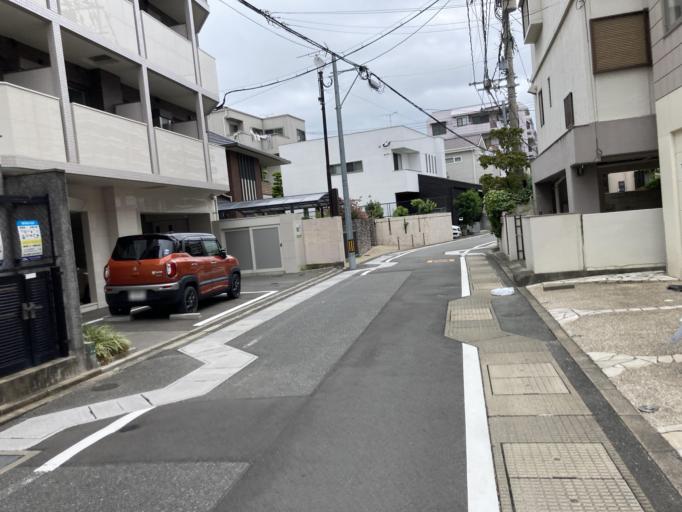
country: JP
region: Fukuoka
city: Fukuoka-shi
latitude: 33.5801
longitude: 130.3493
